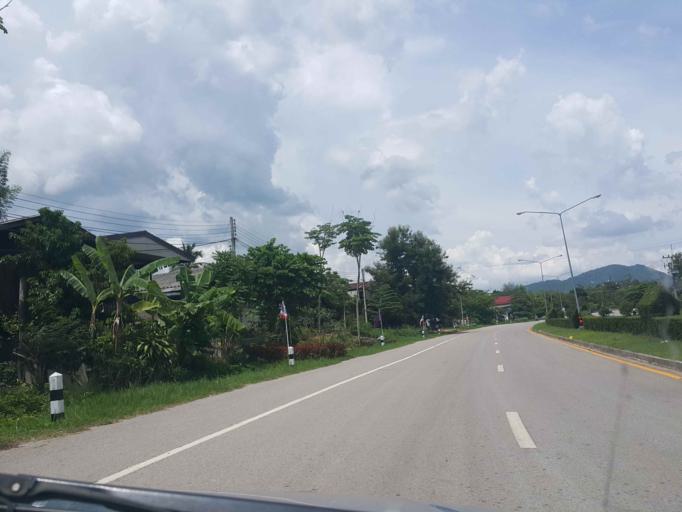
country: TH
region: Nan
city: Ban Luang
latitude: 18.8498
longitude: 100.4317
